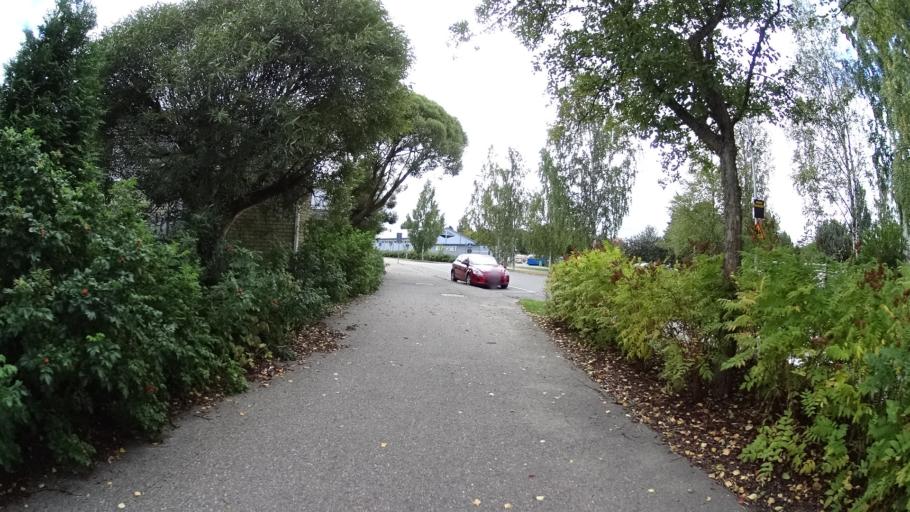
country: FI
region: Uusimaa
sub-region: Helsinki
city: Helsinki
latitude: 60.2594
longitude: 24.9442
